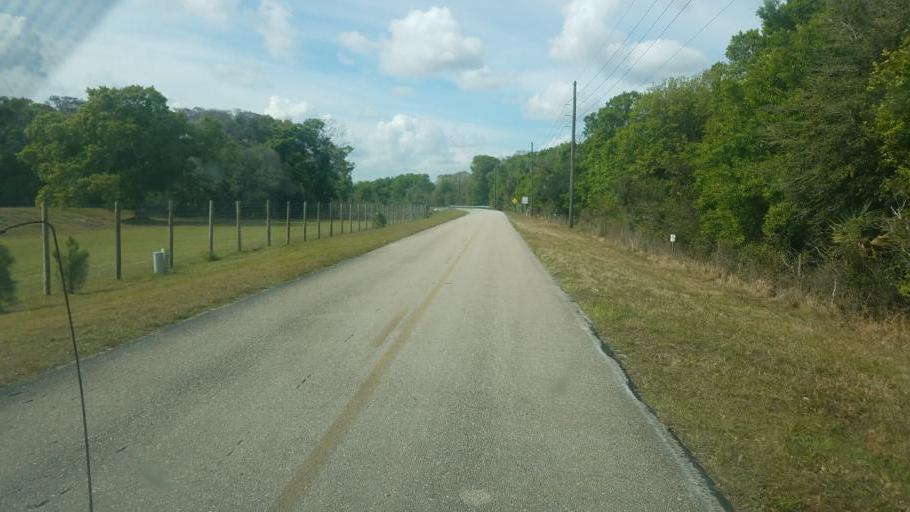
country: US
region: Florida
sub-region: Okeechobee County
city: Cypress Quarters
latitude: 27.5219
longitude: -80.7965
